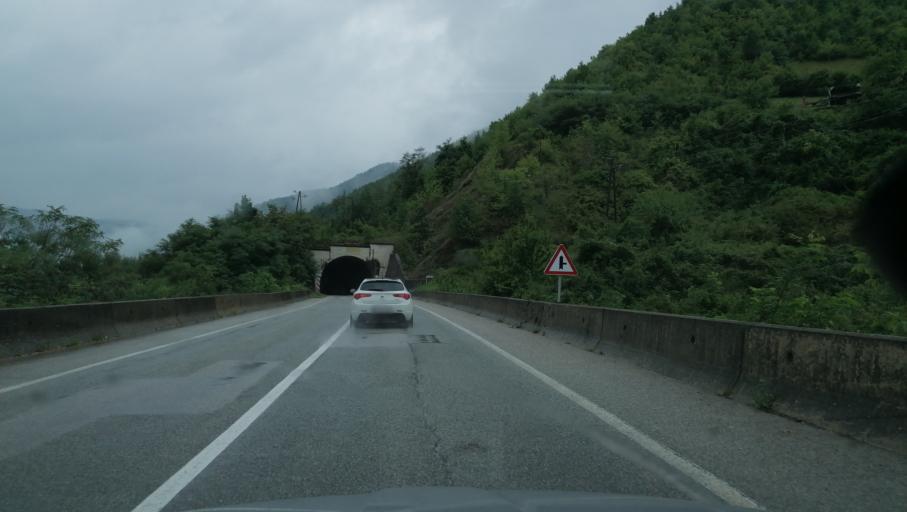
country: BA
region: Republika Srpska
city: Visegrad
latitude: 43.7271
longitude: 19.1690
